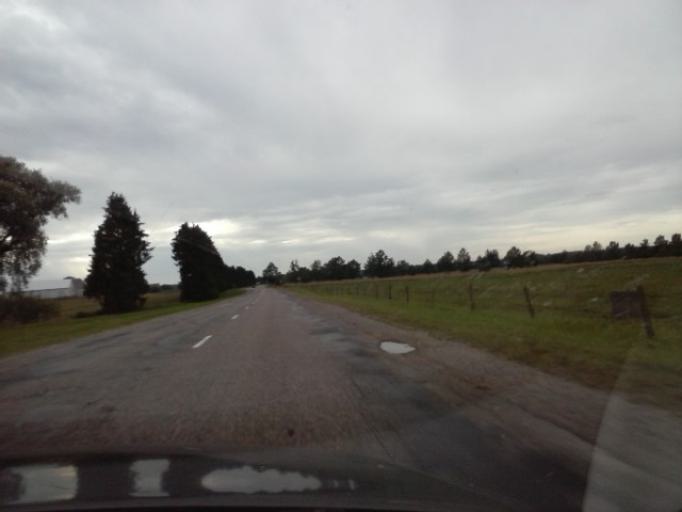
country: LV
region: Skrunda
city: Skrunda
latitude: 56.8440
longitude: 22.2306
